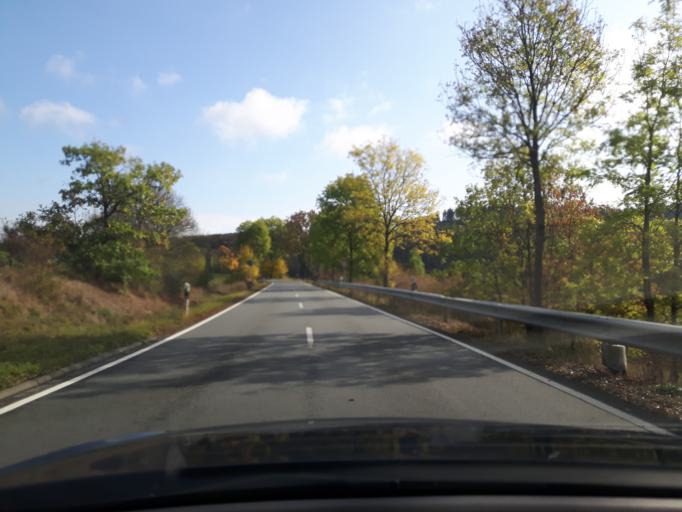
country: DE
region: North Rhine-Westphalia
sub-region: Regierungsbezirk Arnsberg
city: Bad Berleburg
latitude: 51.0186
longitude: 8.4536
